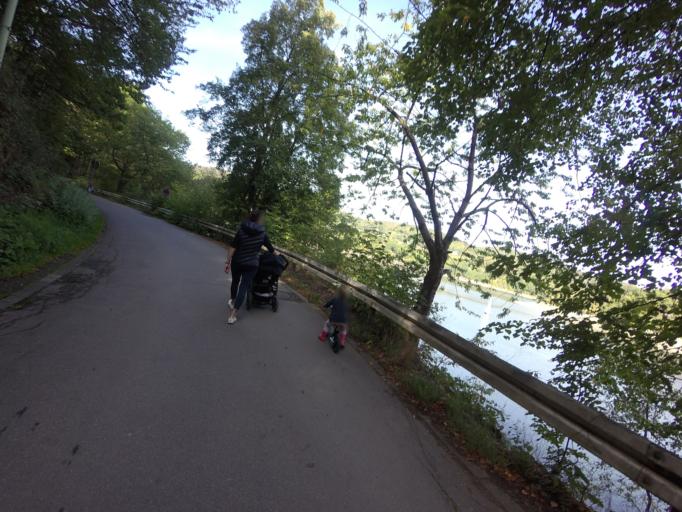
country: DE
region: North Rhine-Westphalia
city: Heimbach
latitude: 50.6180
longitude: 6.3867
